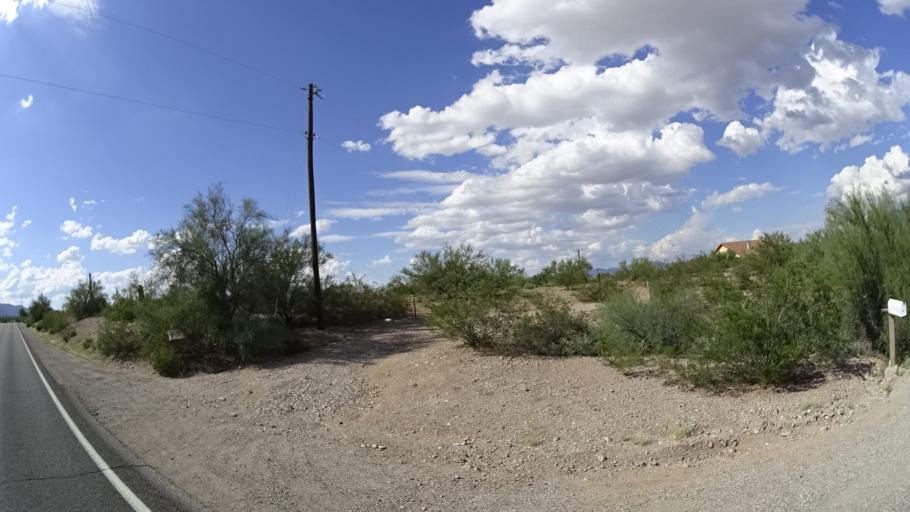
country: US
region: Arizona
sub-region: Pima County
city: Flowing Wells
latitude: 32.2798
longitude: -111.0396
